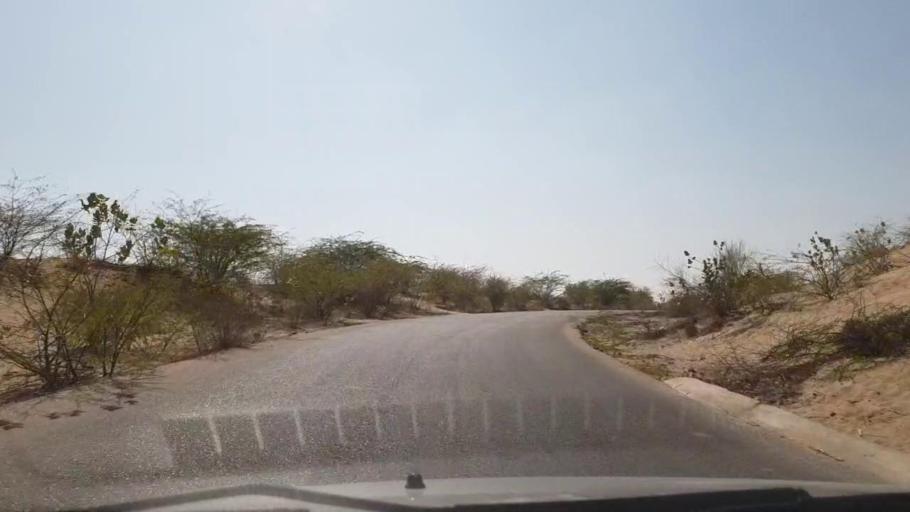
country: PK
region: Sindh
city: Mithi
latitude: 24.5902
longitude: 69.7122
